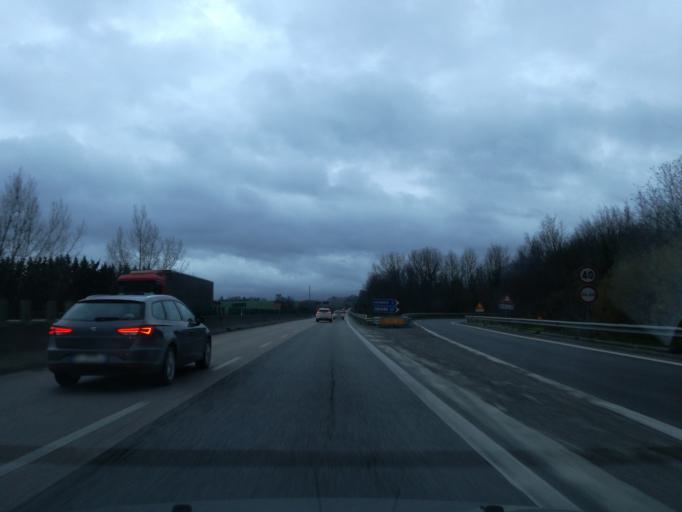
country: IT
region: Umbria
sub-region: Provincia di Perugia
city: Via Lippia
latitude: 43.1012
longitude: 12.4765
